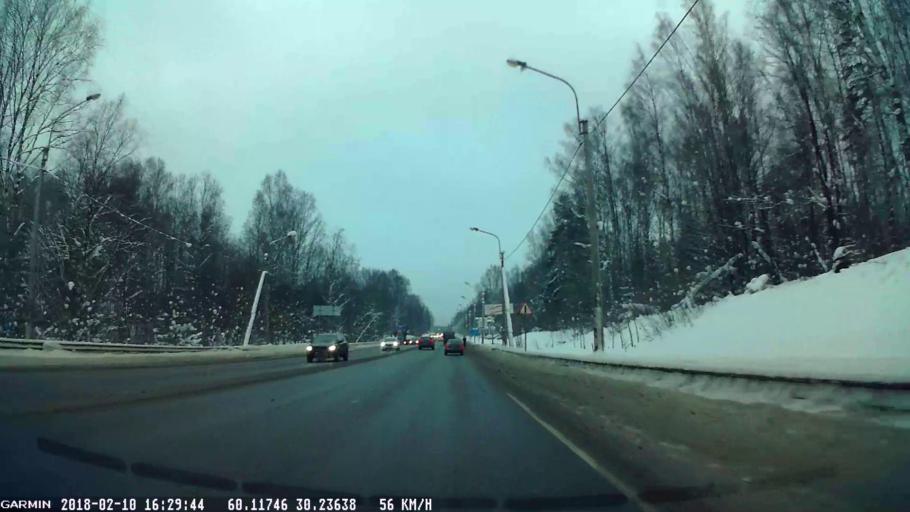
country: RU
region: St.-Petersburg
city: Levashovo
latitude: 60.1183
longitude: 30.2356
